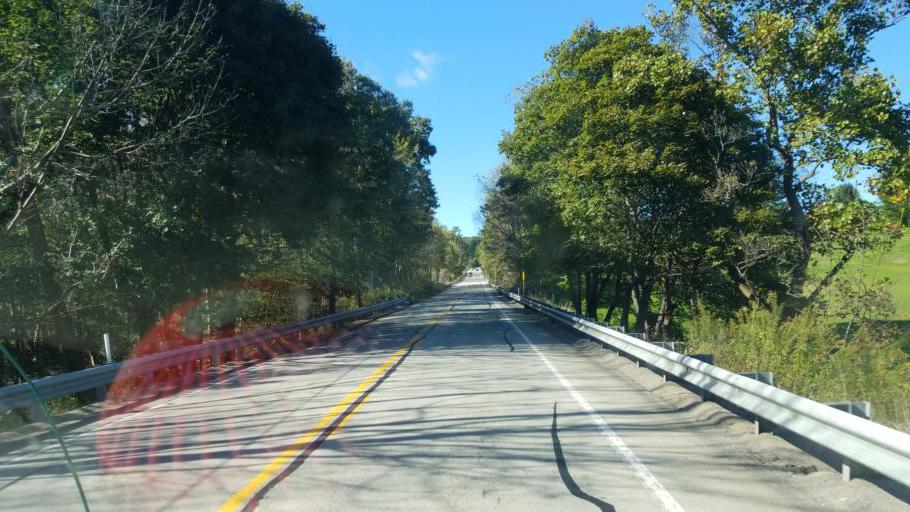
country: US
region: Pennsylvania
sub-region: Somerset County
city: Boswell
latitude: 40.1690
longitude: -79.1038
